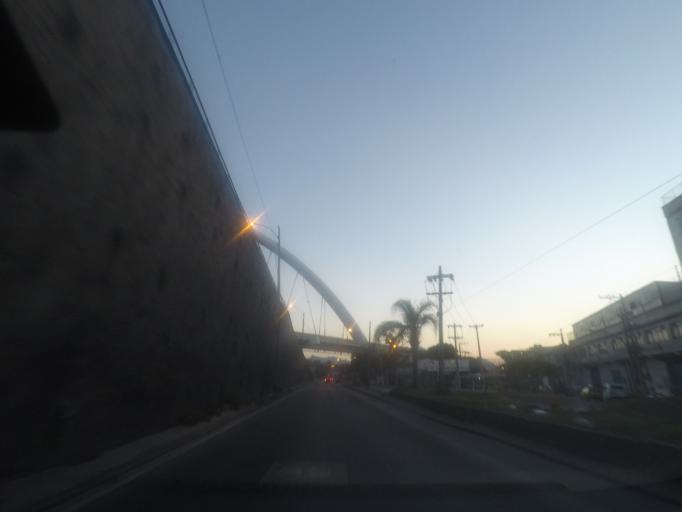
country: BR
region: Rio de Janeiro
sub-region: Rio De Janeiro
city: Rio de Janeiro
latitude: -22.8491
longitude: -43.2476
